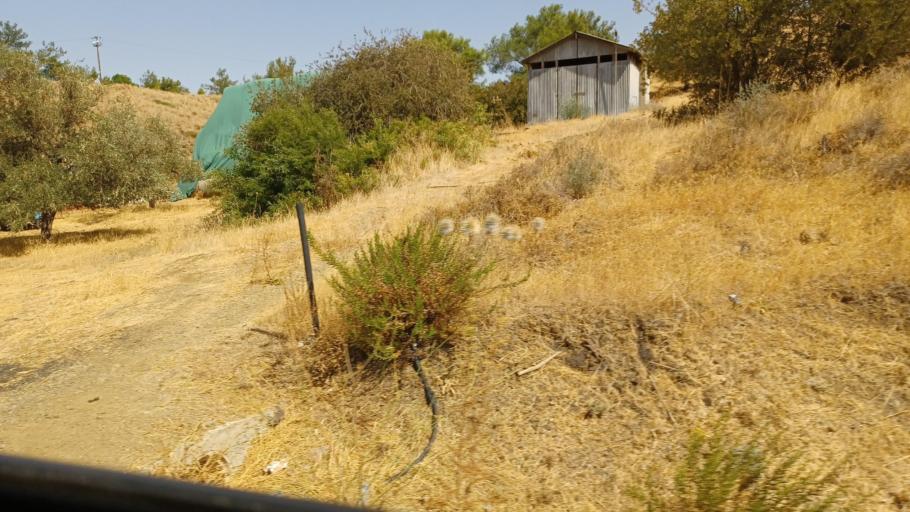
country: CY
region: Lefkosia
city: Kakopetria
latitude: 35.0466
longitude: 32.8979
